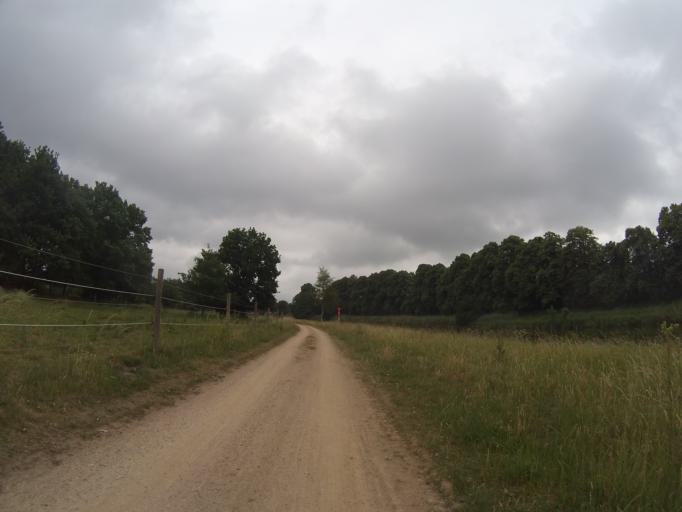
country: DE
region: Lower Saxony
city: Meppen
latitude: 52.7027
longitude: 7.2833
